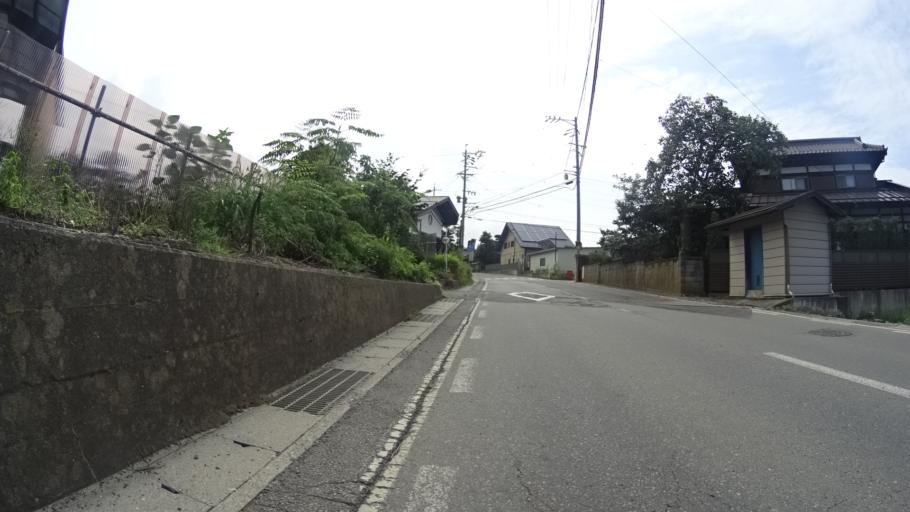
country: JP
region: Nagano
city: Chino
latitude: 35.9559
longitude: 138.2346
